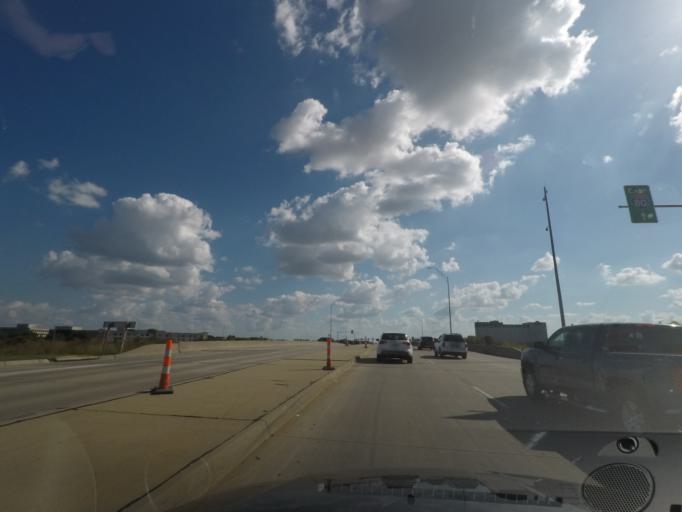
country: US
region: Iowa
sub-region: Dallas County
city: Waukee
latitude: 41.5925
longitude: -93.8091
